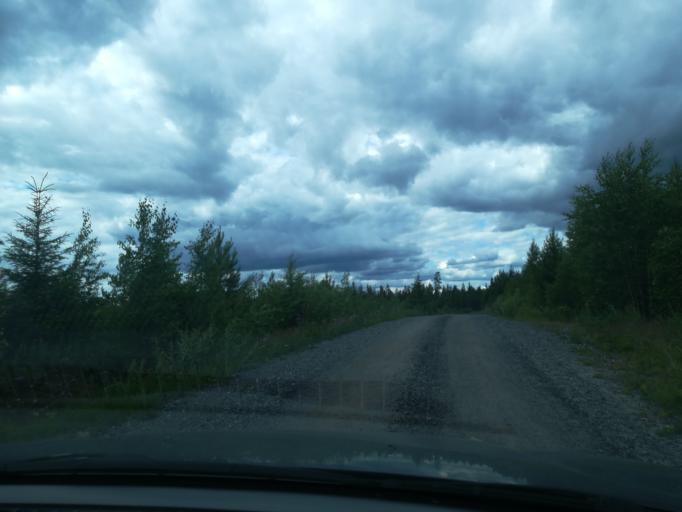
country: FI
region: Southern Savonia
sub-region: Mikkeli
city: Mikkeli
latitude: 61.6710
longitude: 27.1184
